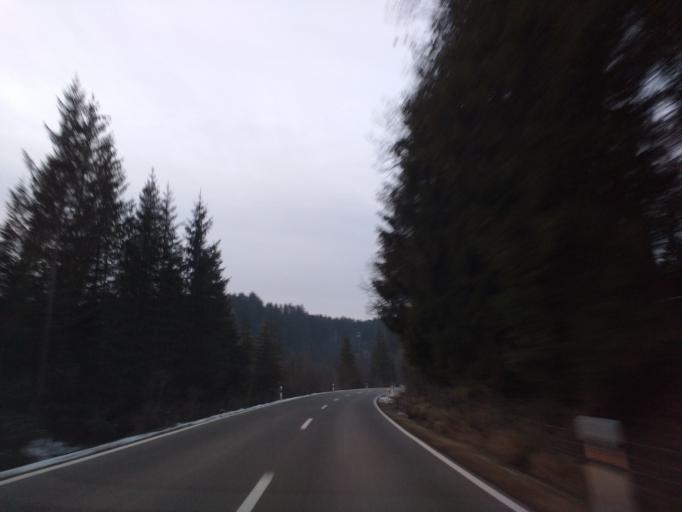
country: DE
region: Bavaria
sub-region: Swabia
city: Halblech
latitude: 47.6484
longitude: 10.7973
